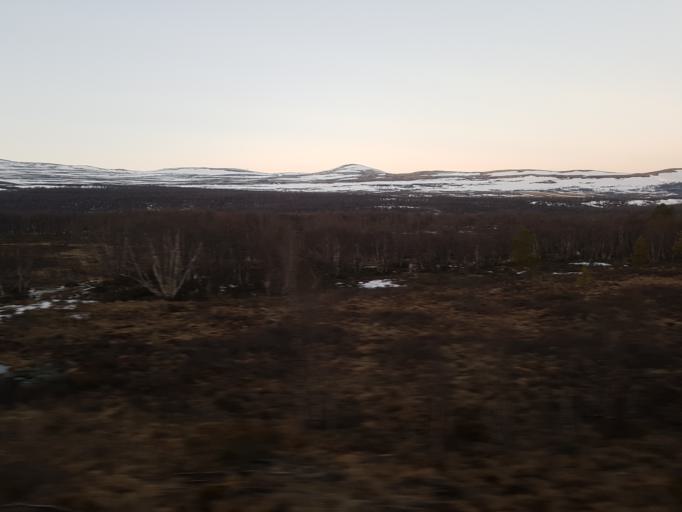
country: NO
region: Oppland
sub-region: Dovre
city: Dombas
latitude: 62.1031
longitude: 9.2213
